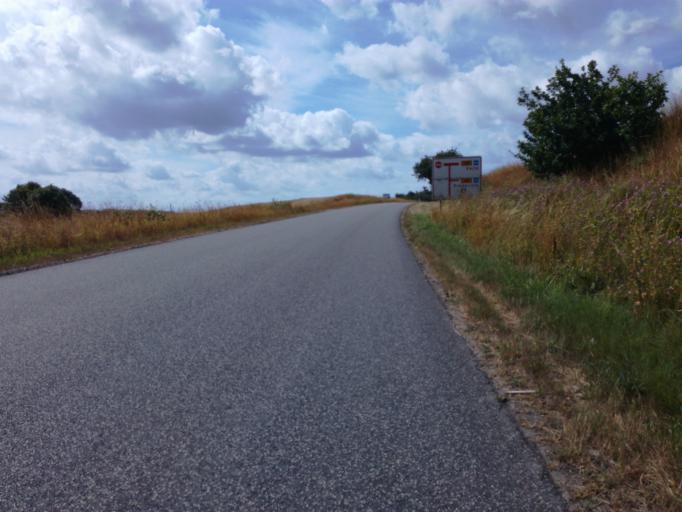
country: DK
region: South Denmark
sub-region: Fredericia Kommune
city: Fredericia
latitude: 55.6272
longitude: 9.7350
